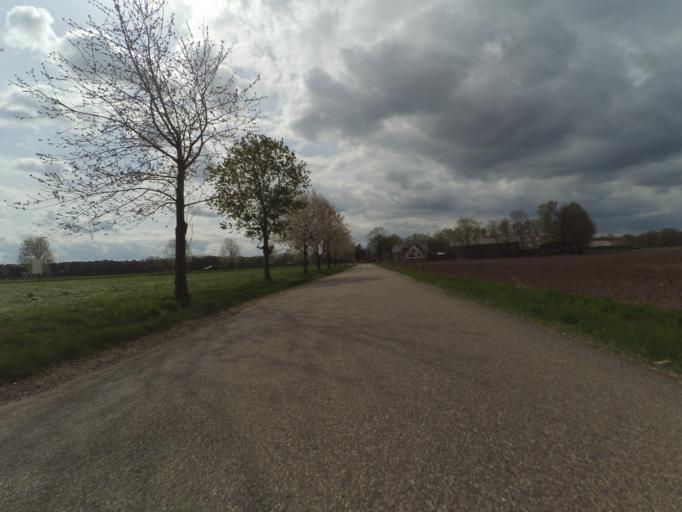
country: NL
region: Gelderland
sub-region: Gemeente Ede
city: Wekerom
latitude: 52.0987
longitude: 5.7360
